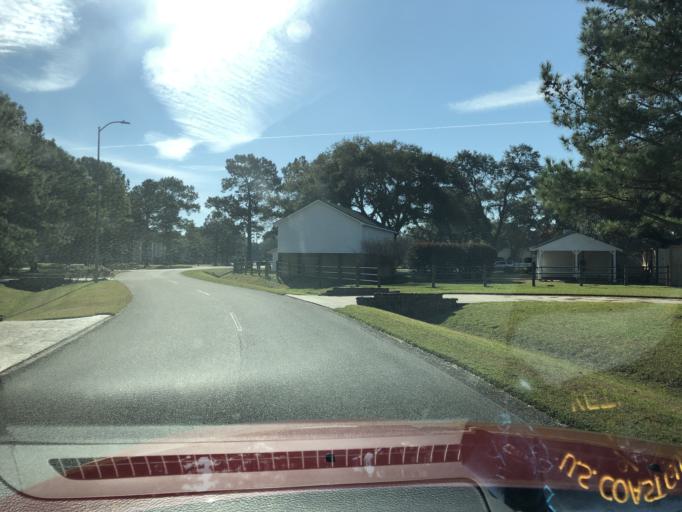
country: US
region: Texas
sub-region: Harris County
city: Tomball
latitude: 30.0437
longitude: -95.5618
